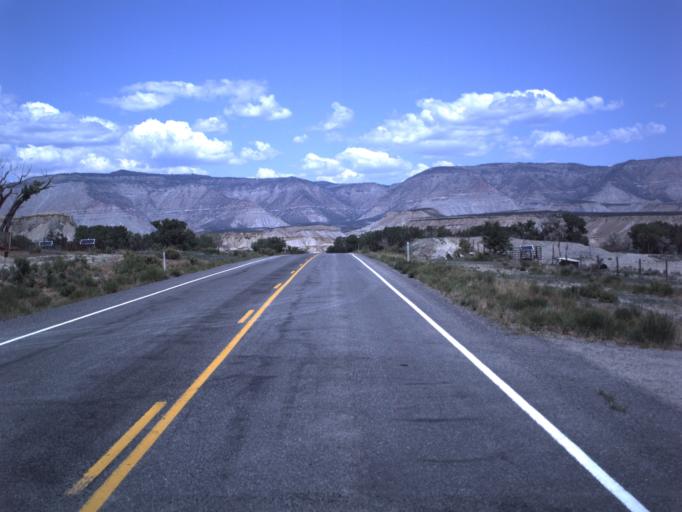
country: US
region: Utah
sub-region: Emery County
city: Orangeville
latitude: 39.2253
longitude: -111.0716
